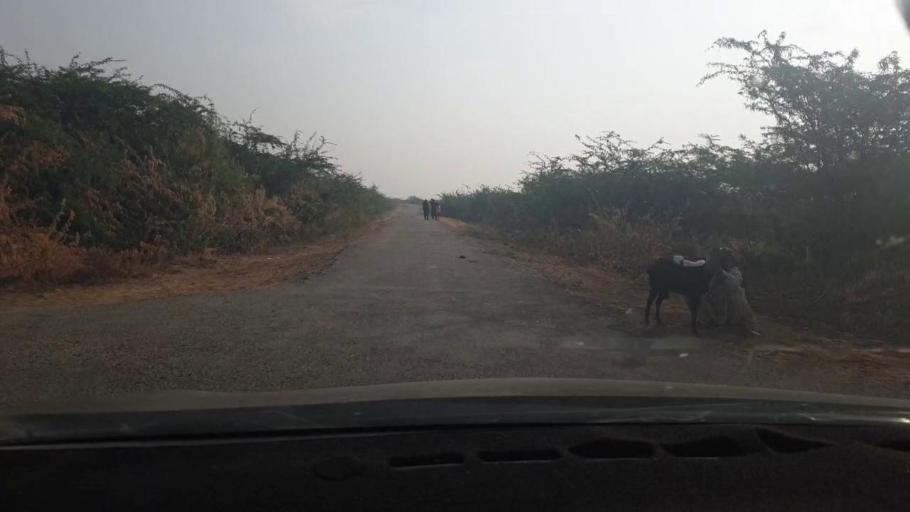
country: PK
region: Sindh
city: Malir Cantonment
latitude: 24.9560
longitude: 67.4511
